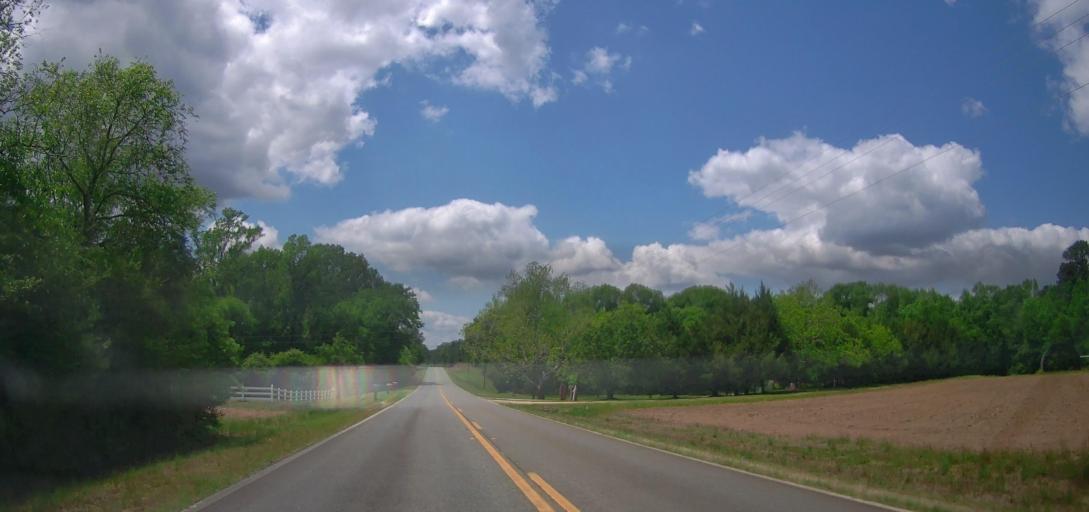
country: US
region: Georgia
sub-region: Laurens County
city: East Dublin
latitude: 32.5248
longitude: -82.7379
